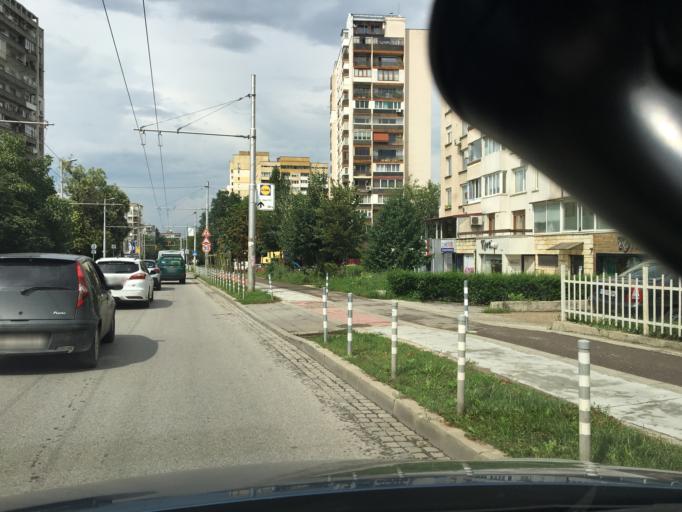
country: BG
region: Sofia-Capital
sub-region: Stolichna Obshtina
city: Sofia
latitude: 42.6676
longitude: 23.2763
